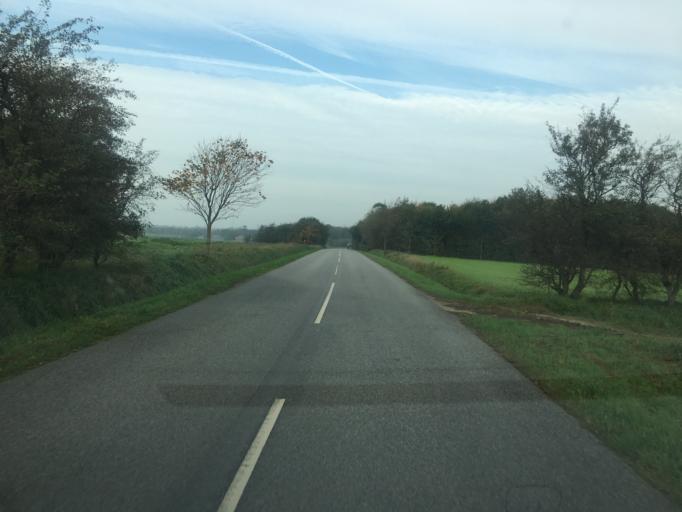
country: DK
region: South Denmark
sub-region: Tonder Kommune
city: Toftlund
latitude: 55.1126
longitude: 9.0845
